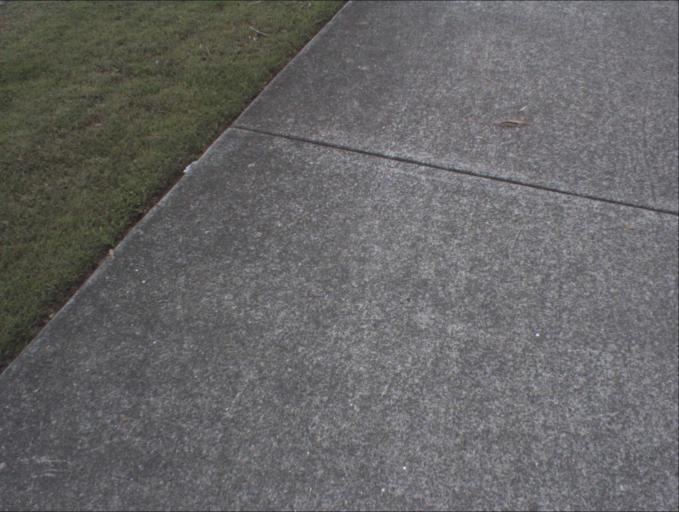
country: AU
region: Queensland
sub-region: Logan
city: Waterford West
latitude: -27.6873
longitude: 153.1509
